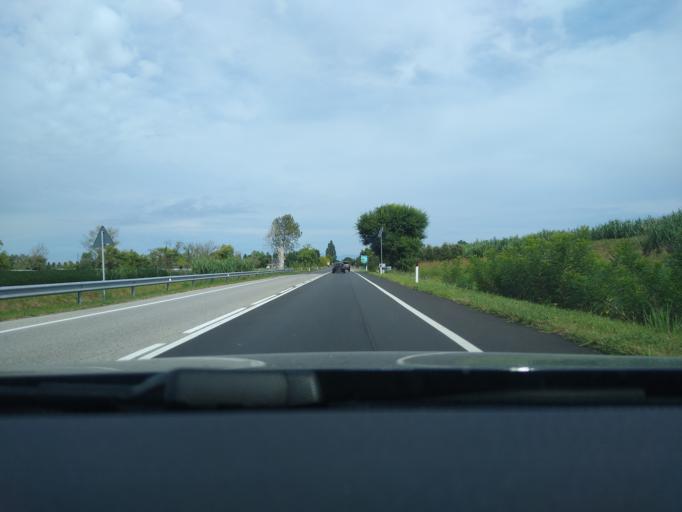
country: IT
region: Friuli Venezia Giulia
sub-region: Provincia di Udine
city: Pertegada
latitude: 45.6795
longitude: 13.0476
